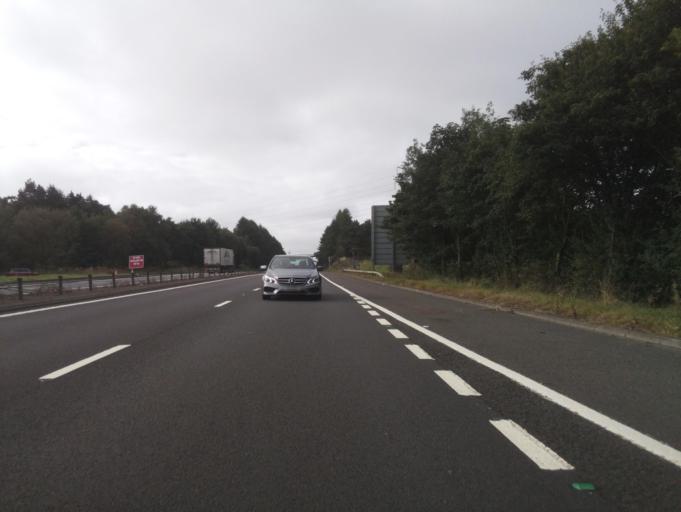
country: GB
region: Scotland
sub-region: Falkirk
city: Larbert
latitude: 56.0269
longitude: -3.8602
